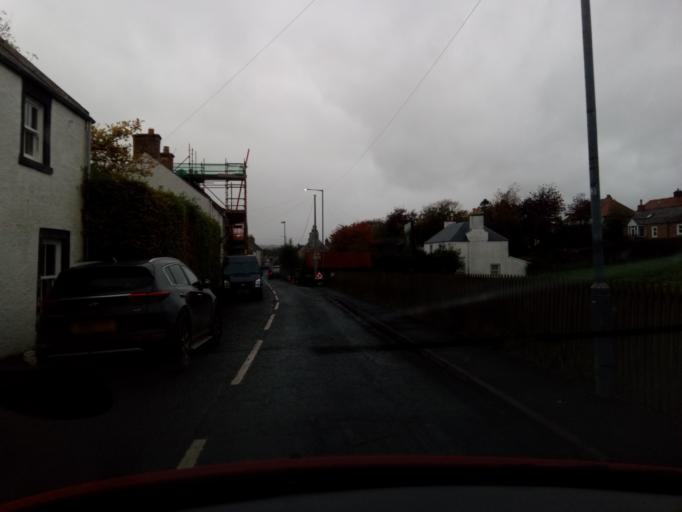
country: GB
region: Scotland
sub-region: The Scottish Borders
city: Melrose
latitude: 55.5168
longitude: -2.7415
